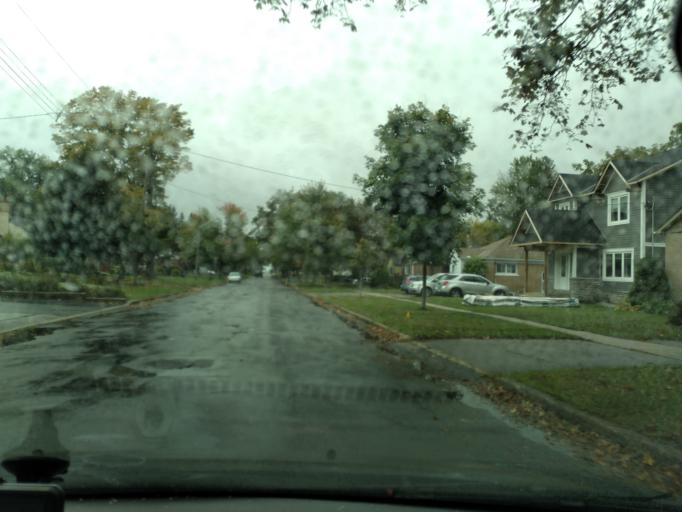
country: CA
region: Ontario
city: Barrie
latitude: 44.3959
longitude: -79.6773
